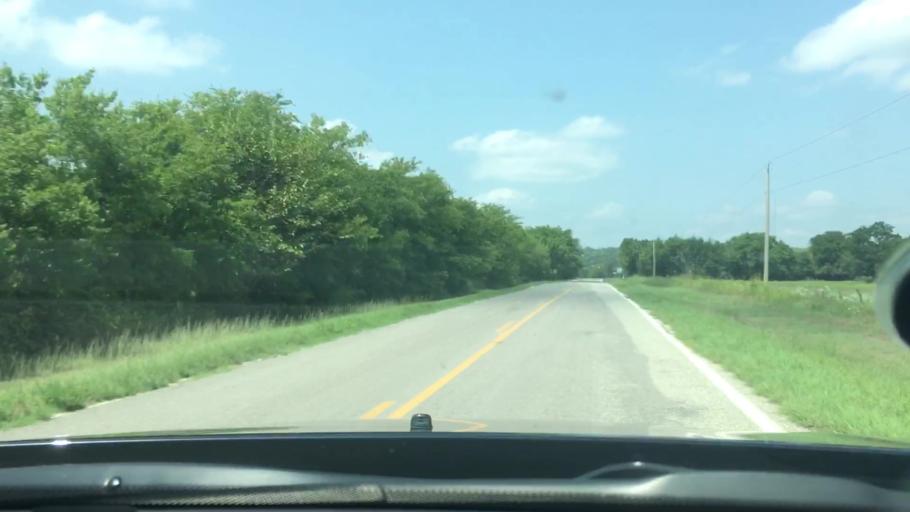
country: US
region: Oklahoma
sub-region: Johnston County
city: Tishomingo
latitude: 34.4096
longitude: -96.4967
